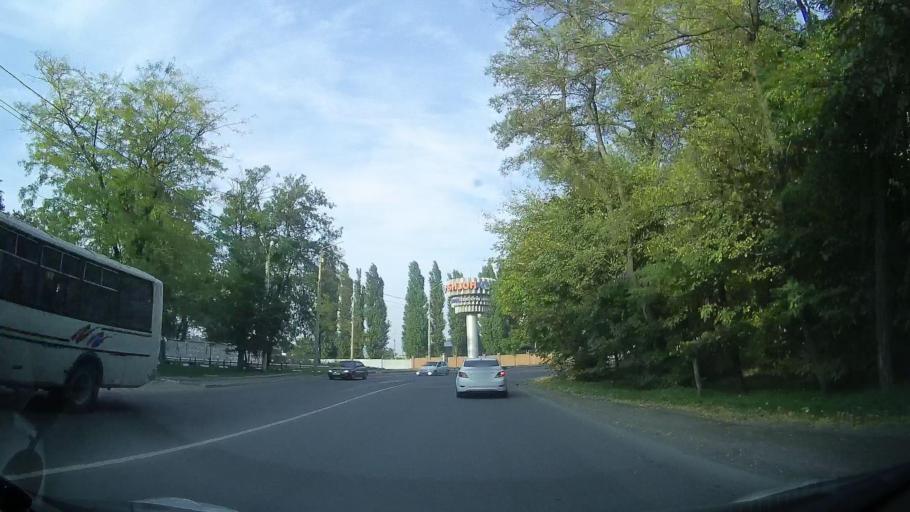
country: RU
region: Rostov
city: Imeni Chkalova
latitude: 47.2779
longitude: 39.7967
